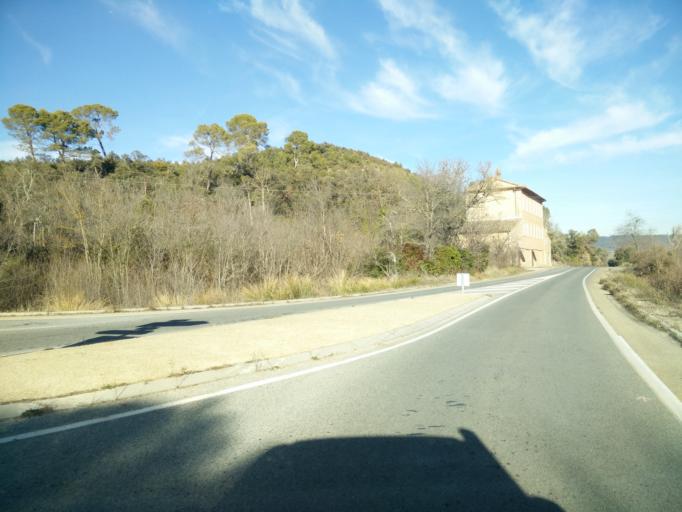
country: FR
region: Provence-Alpes-Cote d'Azur
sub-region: Departement du Var
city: Vidauban
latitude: 43.4318
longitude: 6.4206
